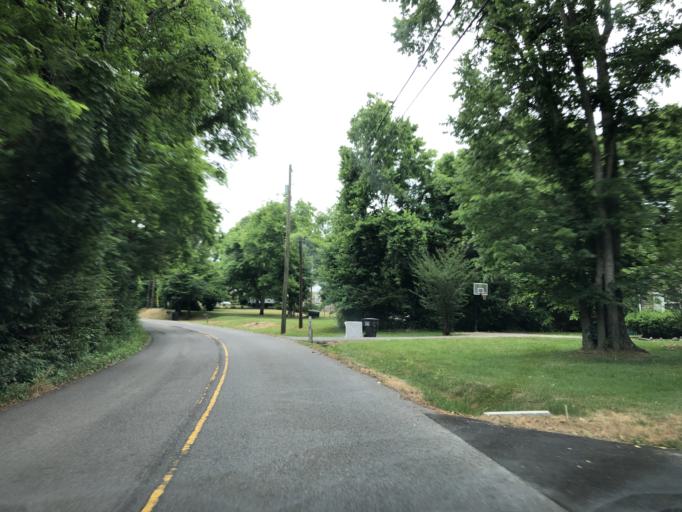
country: US
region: Tennessee
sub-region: Davidson County
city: Goodlettsville
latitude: 36.2861
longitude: -86.7579
